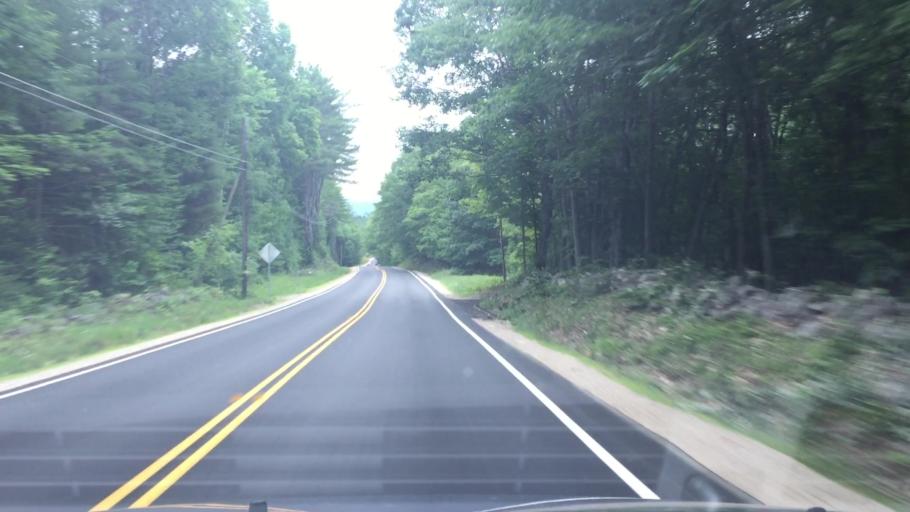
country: US
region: New Hampshire
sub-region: Carroll County
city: Freedom
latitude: 43.8352
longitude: -71.0781
